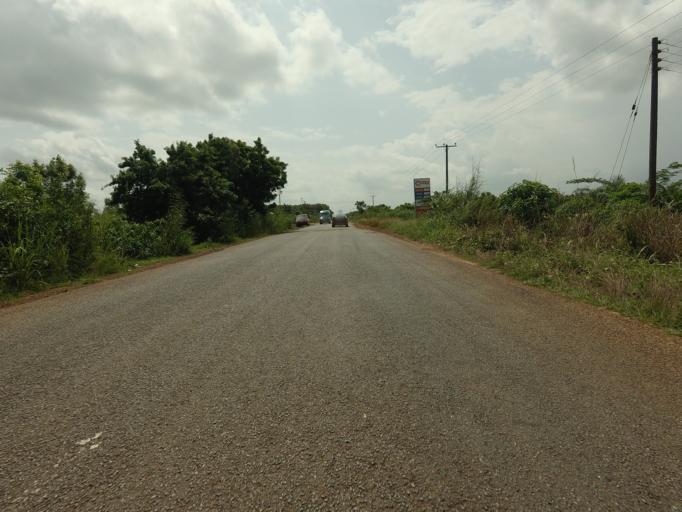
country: TG
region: Maritime
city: Lome
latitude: 6.2140
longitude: 1.0478
